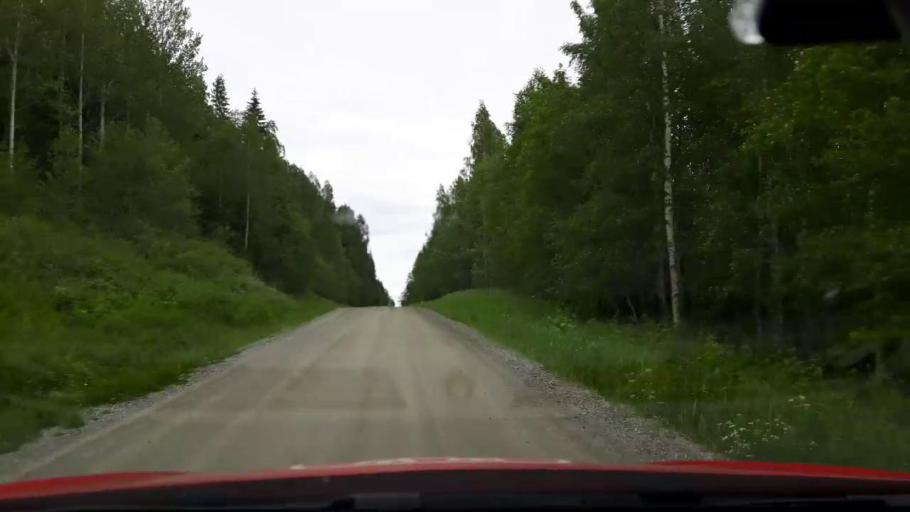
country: SE
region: Jaemtland
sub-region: Ragunda Kommun
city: Hammarstrand
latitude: 63.1876
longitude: 16.1429
